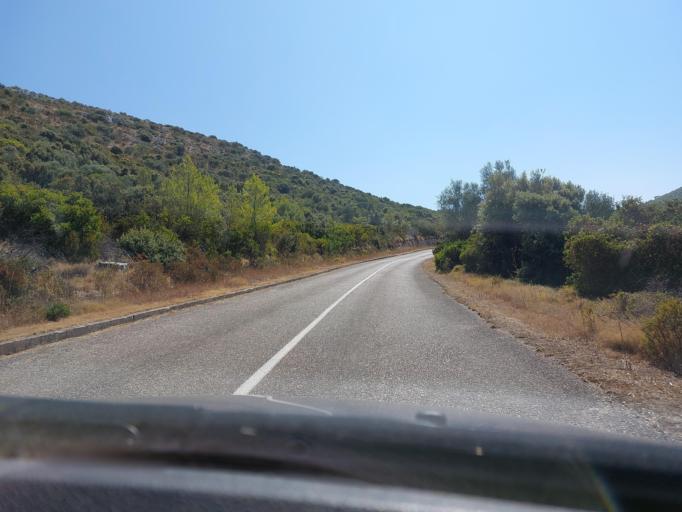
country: HR
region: Dubrovacko-Neretvanska
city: Smokvica
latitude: 42.7482
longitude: 16.8784
